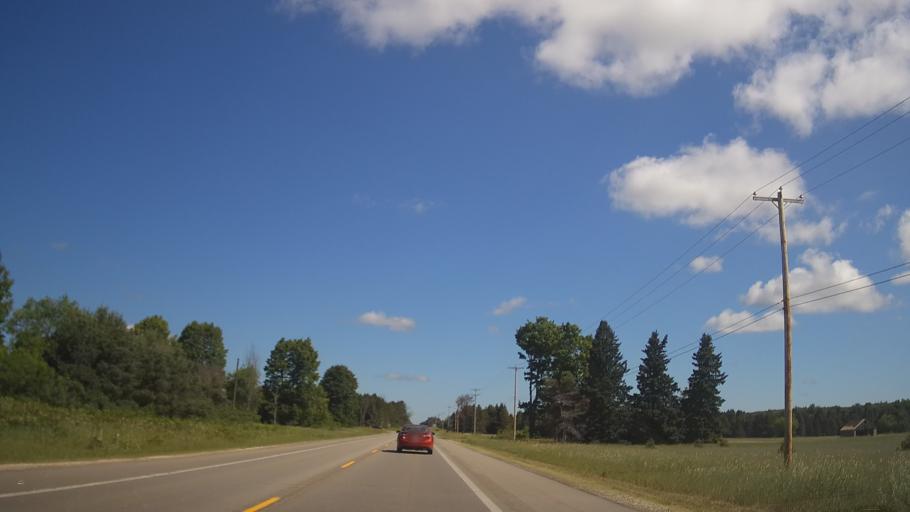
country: US
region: Michigan
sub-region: Cheboygan County
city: Indian River
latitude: 45.4760
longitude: -84.7811
